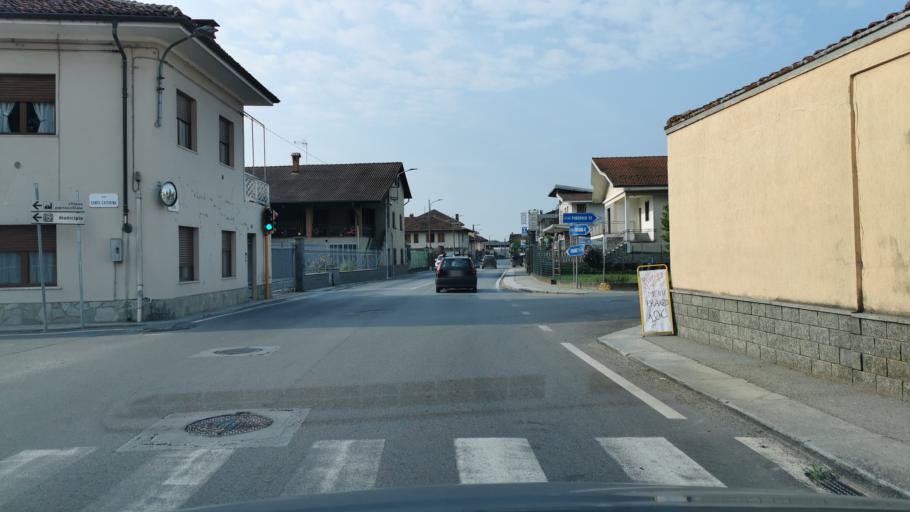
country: IT
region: Piedmont
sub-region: Provincia di Torino
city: Scalenghe
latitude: 44.8883
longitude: 7.4957
